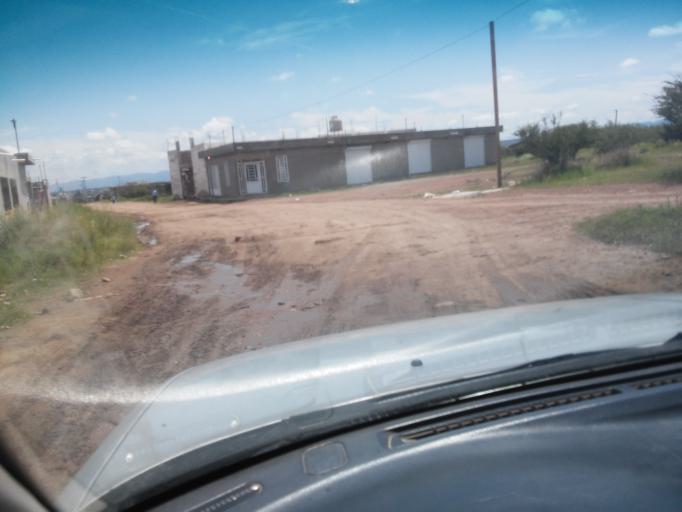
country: MX
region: Durango
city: Victoria de Durango
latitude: 23.9841
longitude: -104.7086
